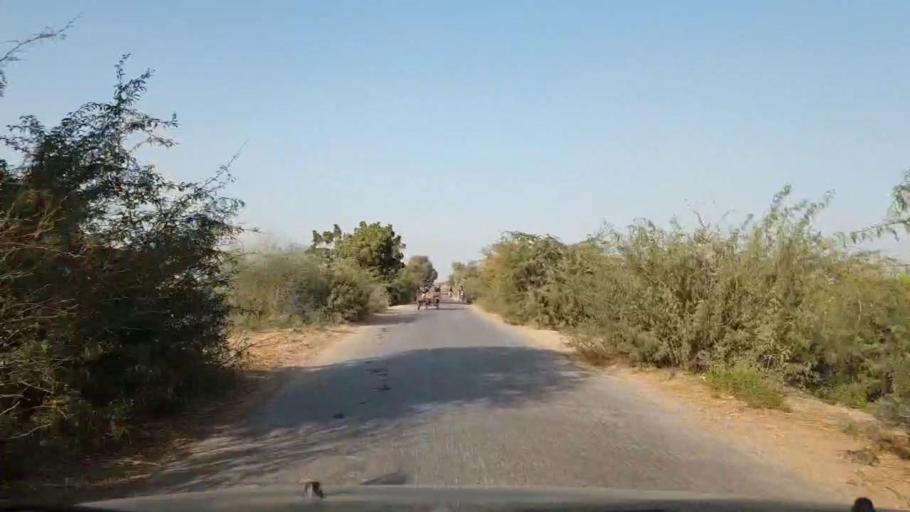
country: PK
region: Sindh
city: Chambar
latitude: 25.2394
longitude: 68.7860
